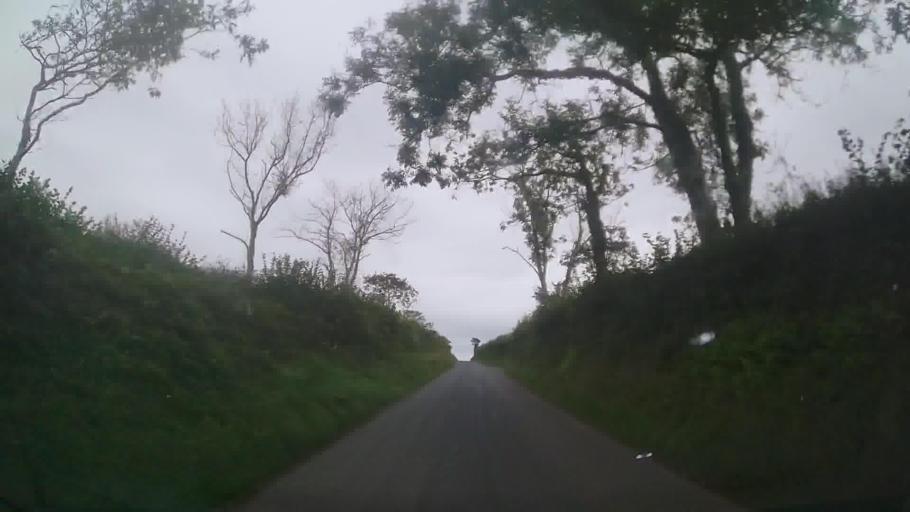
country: GB
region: Wales
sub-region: Carmarthenshire
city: Whitland
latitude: 51.7429
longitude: -4.6235
